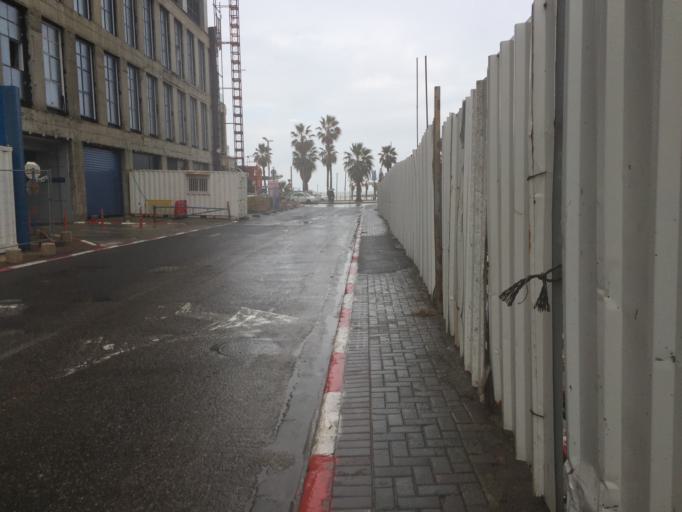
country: IL
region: Tel Aviv
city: Tel Aviv
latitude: 32.0742
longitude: 34.7662
